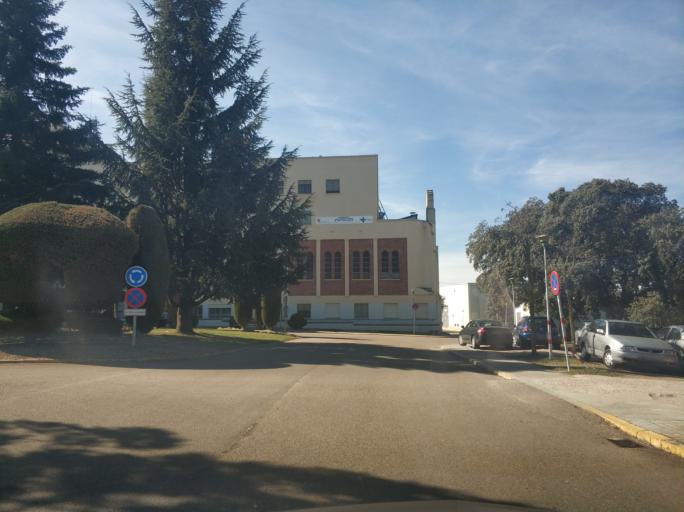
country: ES
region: Castille and Leon
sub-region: Provincia de Salamanca
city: Doninos de Salamanca
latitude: 40.9273
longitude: -5.7400
